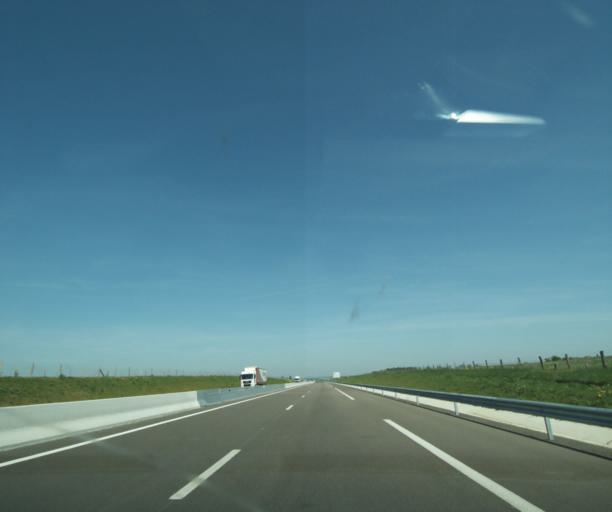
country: FR
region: Bourgogne
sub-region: Departement de la Nievre
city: Saint-Pierre-le-Moutier
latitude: 46.8069
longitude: 3.1207
